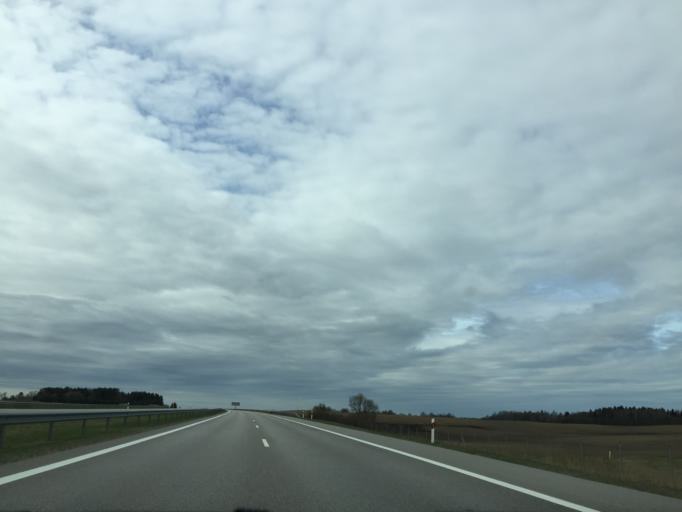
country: LT
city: Silale
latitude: 55.5925
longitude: 22.1337
